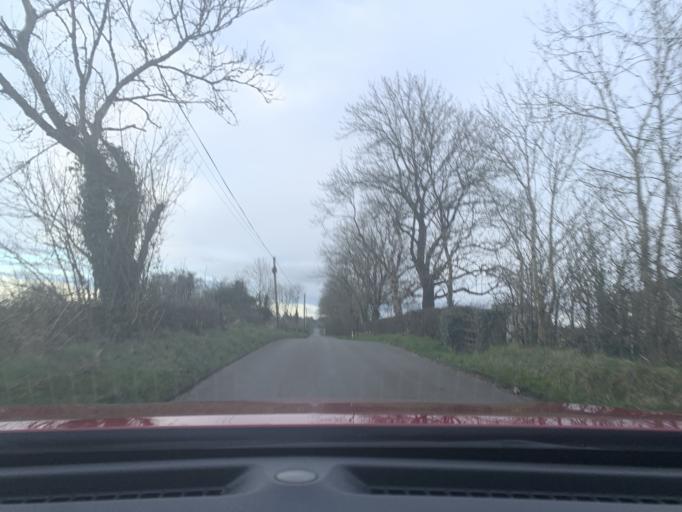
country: IE
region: Connaught
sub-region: Roscommon
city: Ballaghaderreen
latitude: 53.8758
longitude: -8.5604
